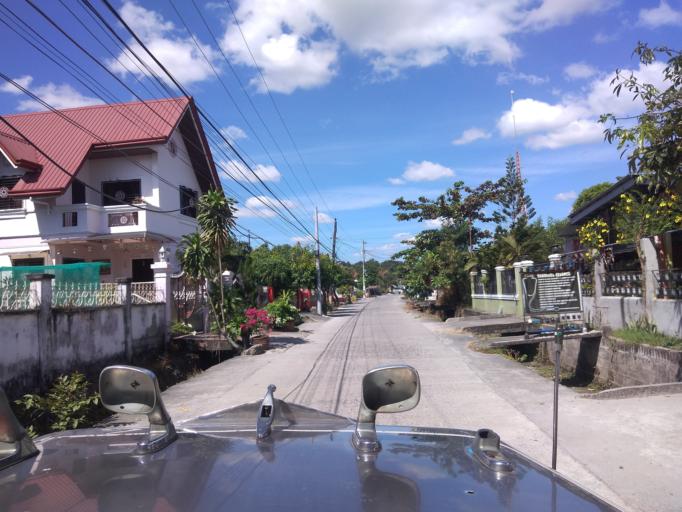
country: PH
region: Central Luzon
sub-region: Province of Pampanga
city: Santa Rita
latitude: 15.0030
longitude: 120.6044
